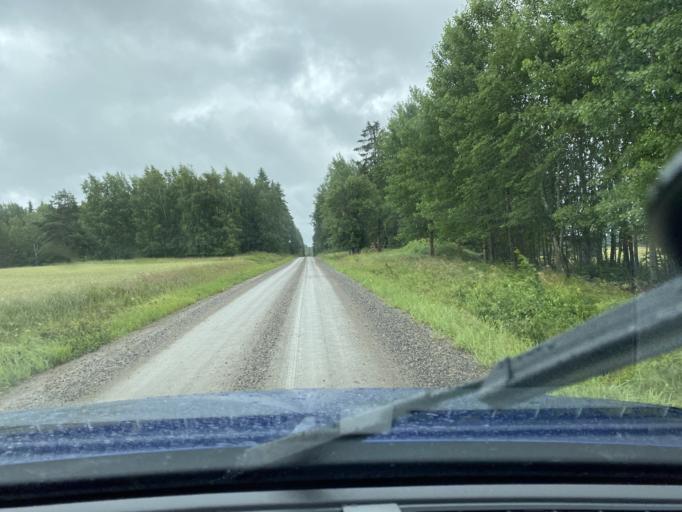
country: FI
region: Pirkanmaa
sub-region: Lounais-Pirkanmaa
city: Punkalaidun
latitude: 61.1498
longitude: 23.2315
